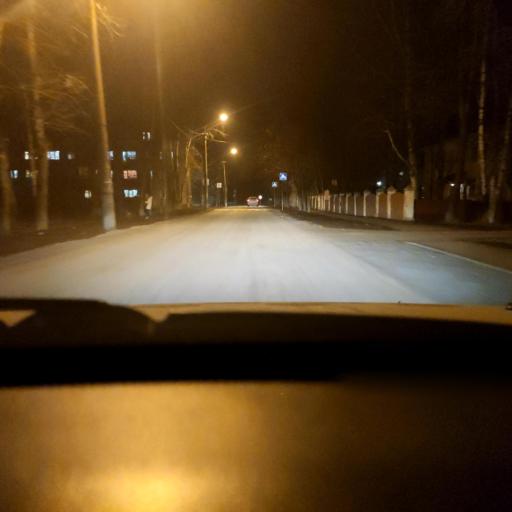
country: RU
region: Perm
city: Polazna
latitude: 58.1496
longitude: 56.4389
